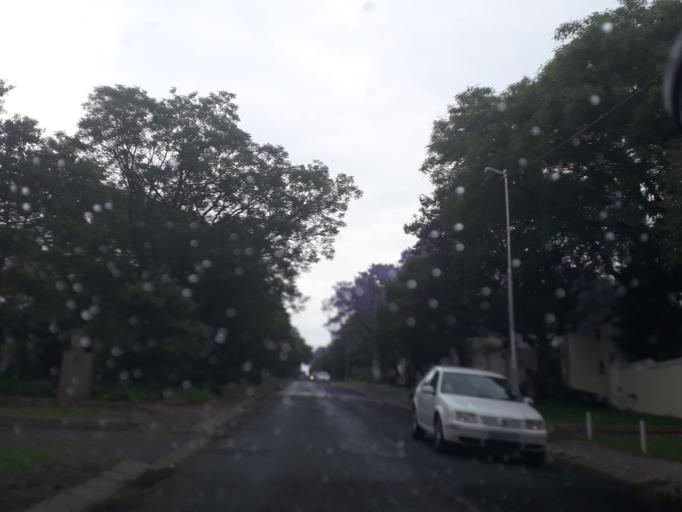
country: ZA
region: Gauteng
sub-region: City of Johannesburg Metropolitan Municipality
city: Johannesburg
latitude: -26.1003
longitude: 28.0299
